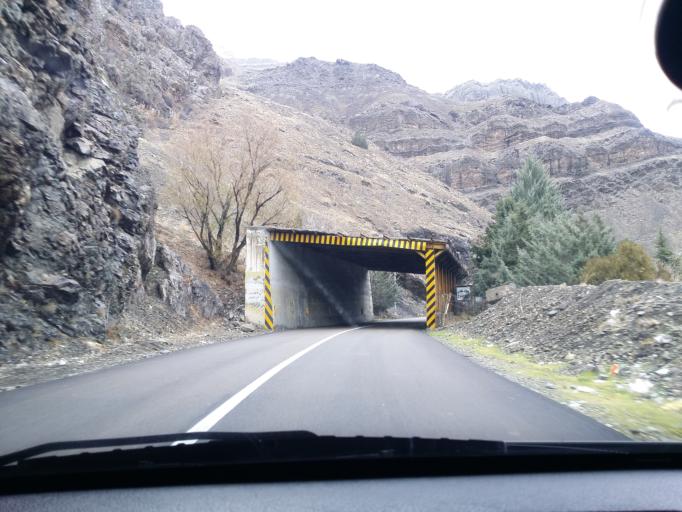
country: IR
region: Alborz
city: Karaj
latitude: 36.0008
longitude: 51.1137
